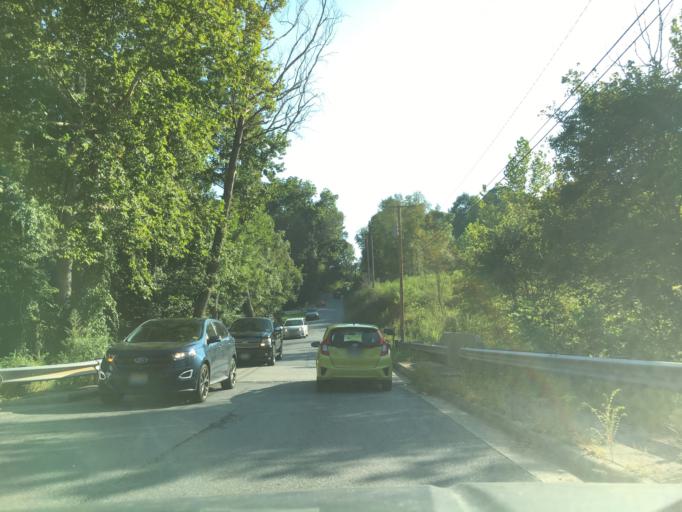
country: US
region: Virginia
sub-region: City of Lynchburg
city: West Lynchburg
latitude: 37.4058
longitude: -79.1893
